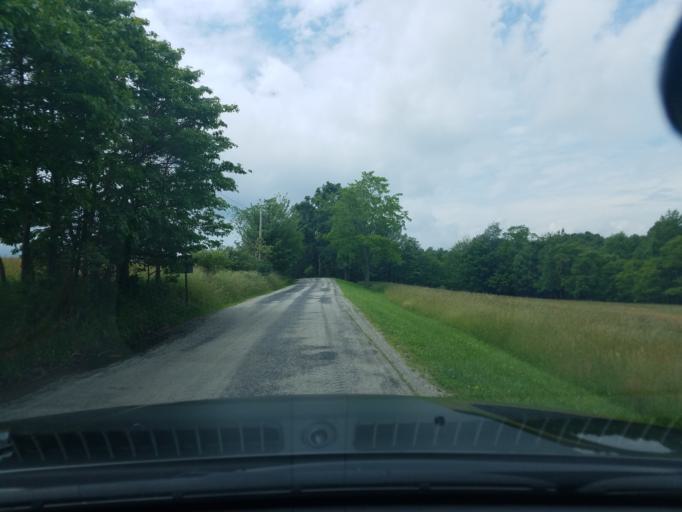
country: US
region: Pennsylvania
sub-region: Fayette County
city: Bear Rocks
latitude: 40.1823
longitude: -79.4027
